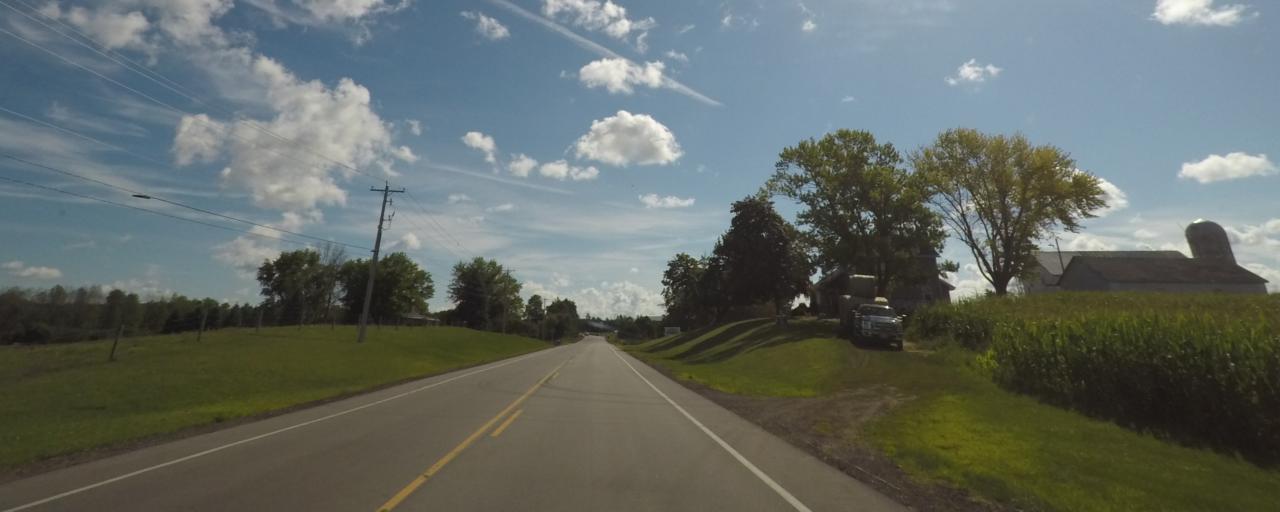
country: US
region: Wisconsin
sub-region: Waukesha County
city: Oconomowoc
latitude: 43.0754
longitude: -88.5491
